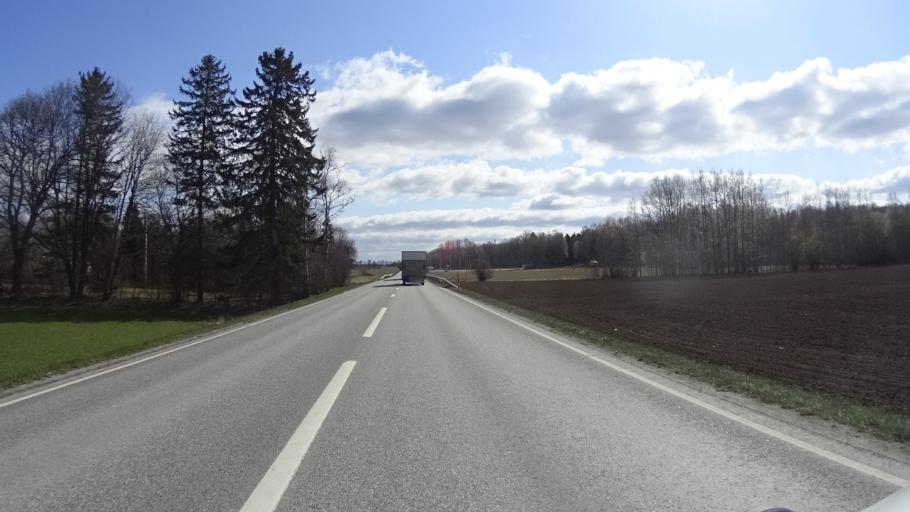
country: SE
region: OEstergoetland
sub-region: Mjolby Kommun
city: Mantorp
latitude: 58.3761
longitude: 15.2777
